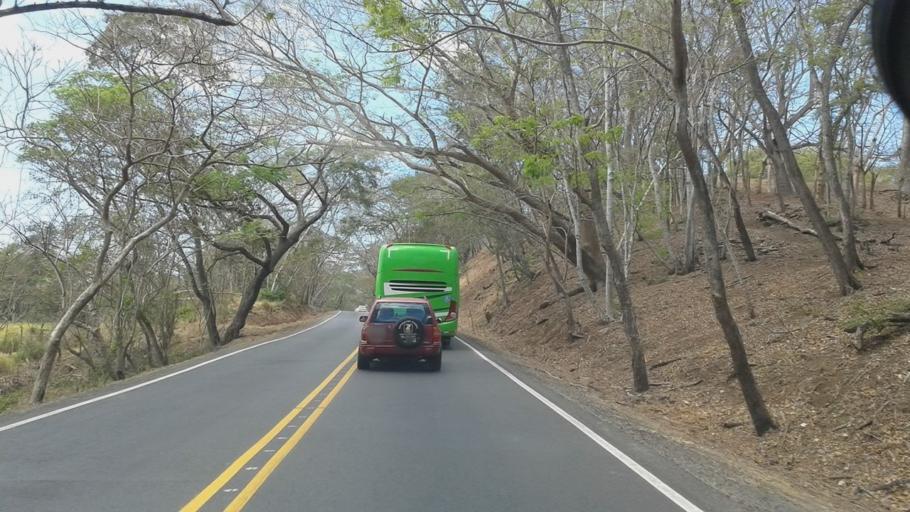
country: CR
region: Puntarenas
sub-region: Canton Central de Puntarenas
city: Puntarenas
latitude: 10.1177
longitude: -84.8962
